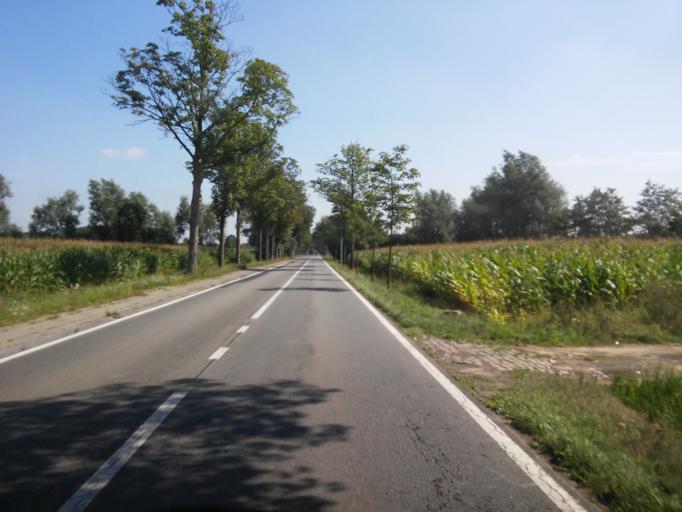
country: BE
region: Flanders
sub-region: Provincie Antwerpen
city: Sint-Amands
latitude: 51.0418
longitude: 4.2318
